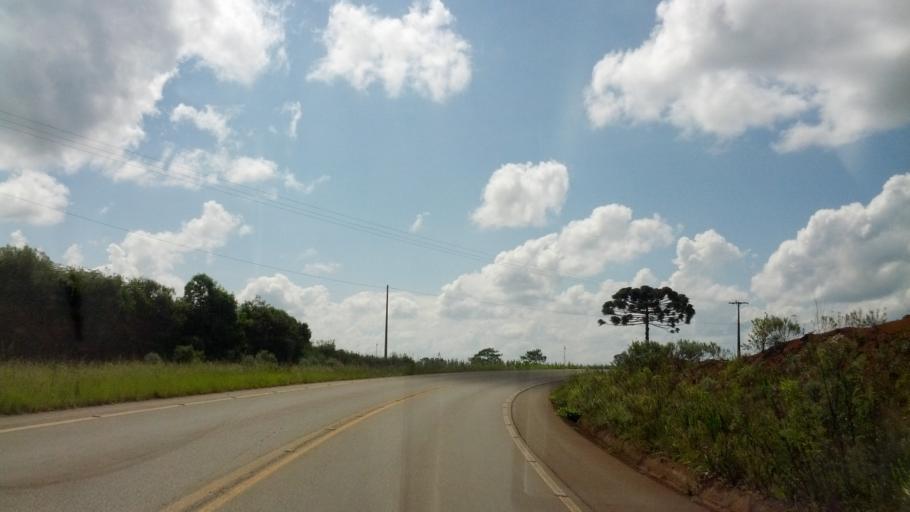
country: BR
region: Rio Grande do Sul
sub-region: Vacaria
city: Estrela
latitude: -27.8084
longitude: -50.8610
